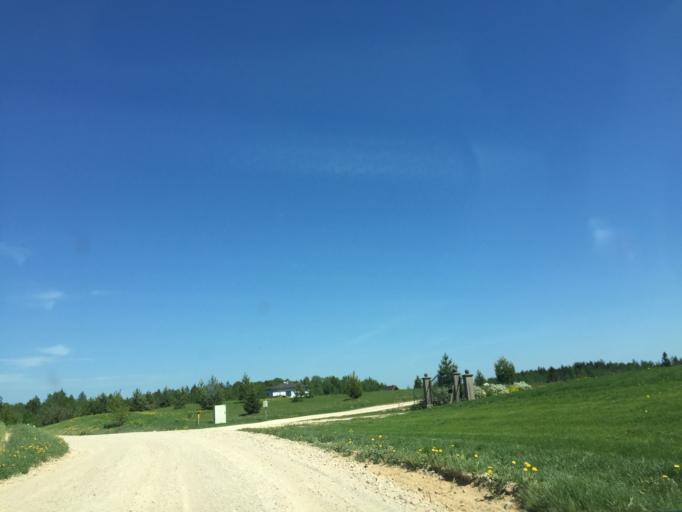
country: LV
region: Ikskile
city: Ikskile
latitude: 56.8678
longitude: 24.5026
